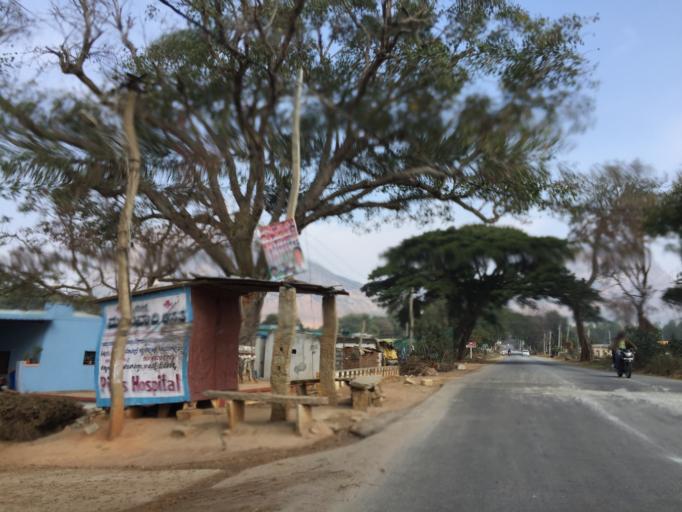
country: IN
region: Karnataka
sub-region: Bangalore Rural
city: Devanhalli
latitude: 13.3400
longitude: 77.6886
